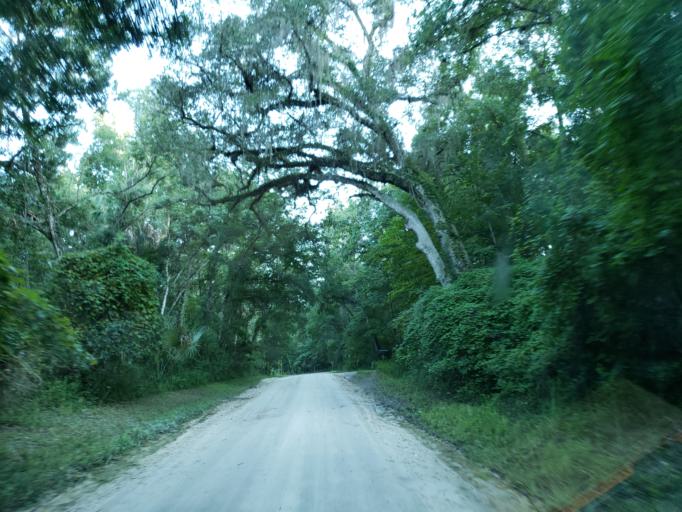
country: US
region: Florida
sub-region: Alachua County
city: Gainesville
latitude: 29.4856
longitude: -82.2770
